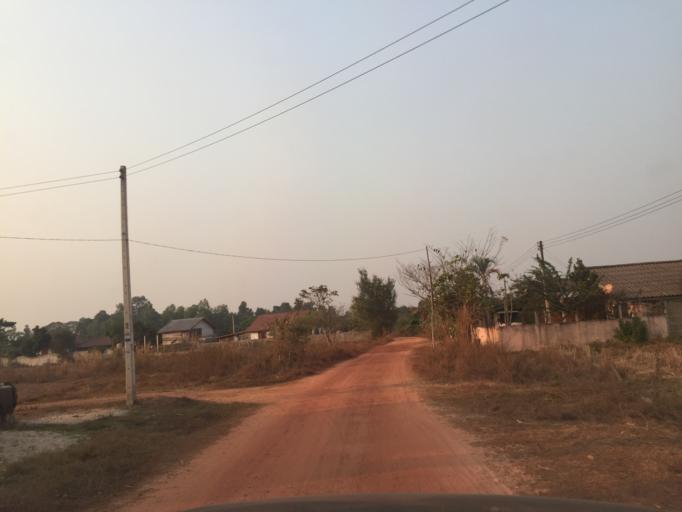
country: LA
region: Vientiane
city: Vientiane
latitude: 18.0590
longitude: 102.5209
